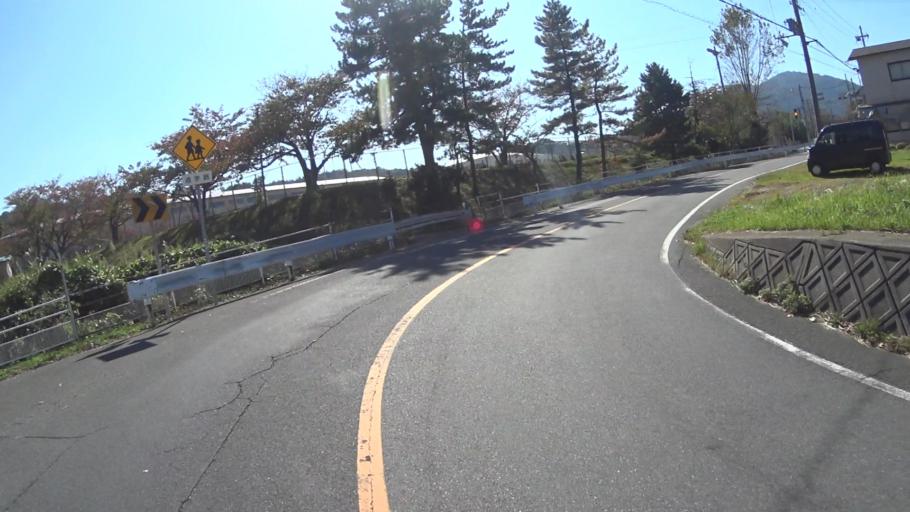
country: JP
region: Kyoto
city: Miyazu
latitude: 35.7532
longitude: 135.1706
